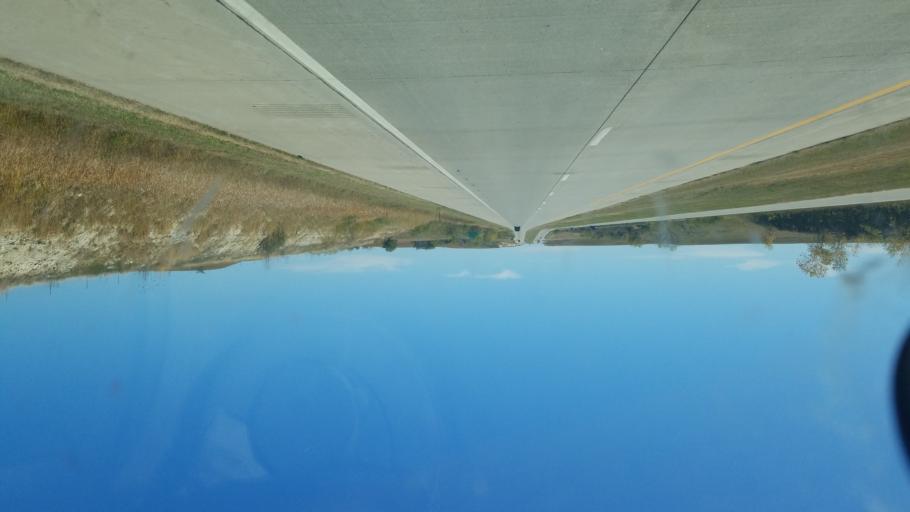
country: US
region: Kansas
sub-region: Riley County
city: Manhattan
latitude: 39.0646
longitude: -96.5658
